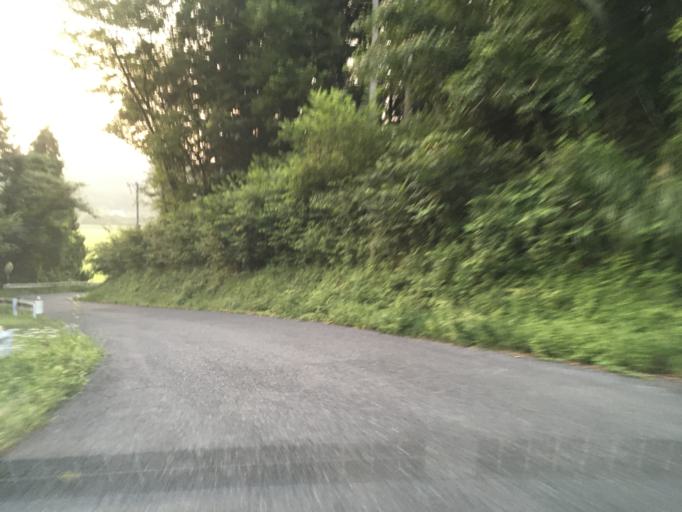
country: JP
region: Iwate
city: Ichinoseki
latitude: 38.8479
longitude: 141.2813
